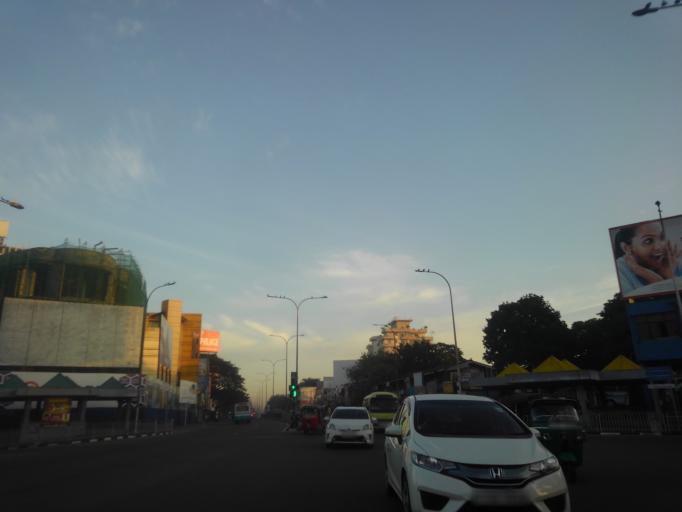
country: LK
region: Western
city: Kolonnawa
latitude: 6.9147
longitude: 79.8776
